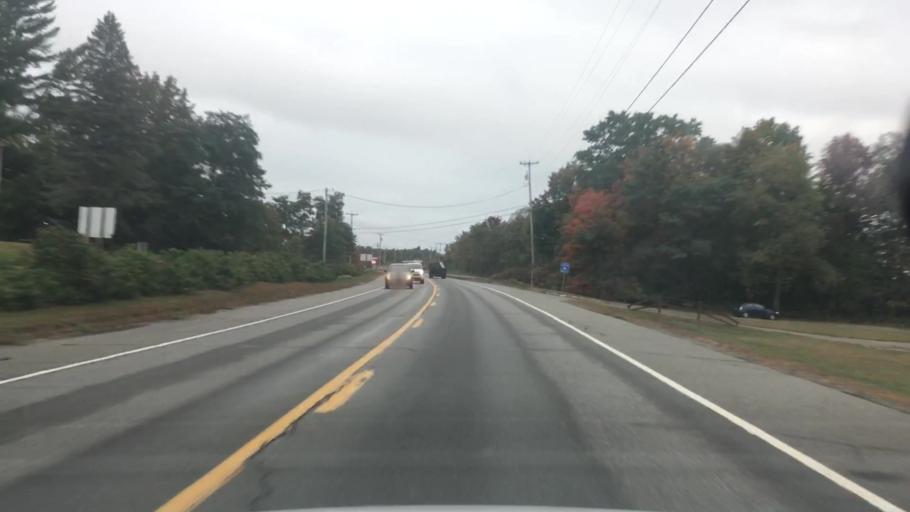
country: US
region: Maine
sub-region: Kennebec County
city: Belgrade
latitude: 44.4421
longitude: -69.8315
